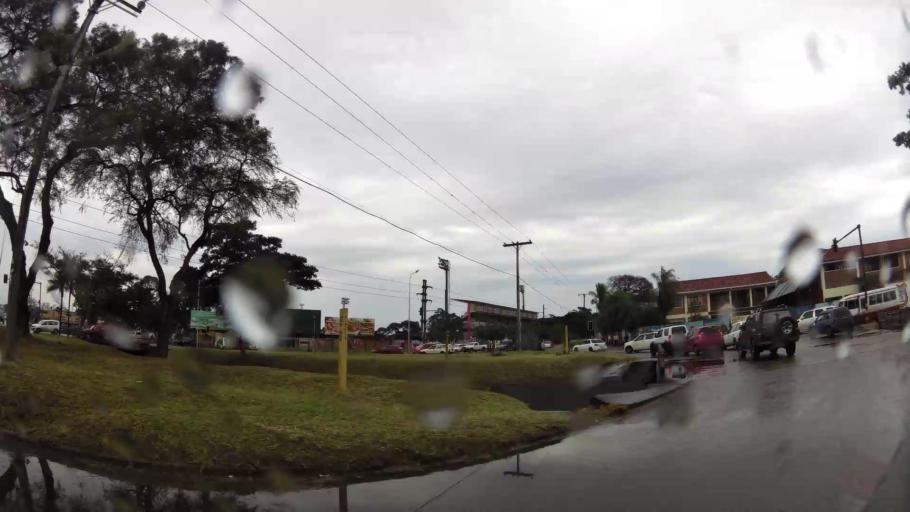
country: BO
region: Santa Cruz
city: Santa Cruz de la Sierra
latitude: -17.8042
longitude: -63.1655
